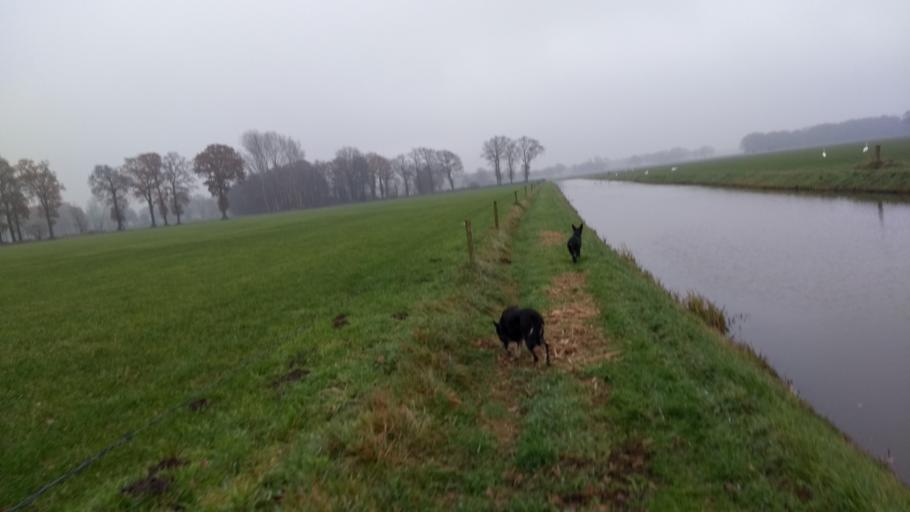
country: NL
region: Overijssel
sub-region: Gemeente Borne
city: Borne
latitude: 52.3425
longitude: 6.7382
